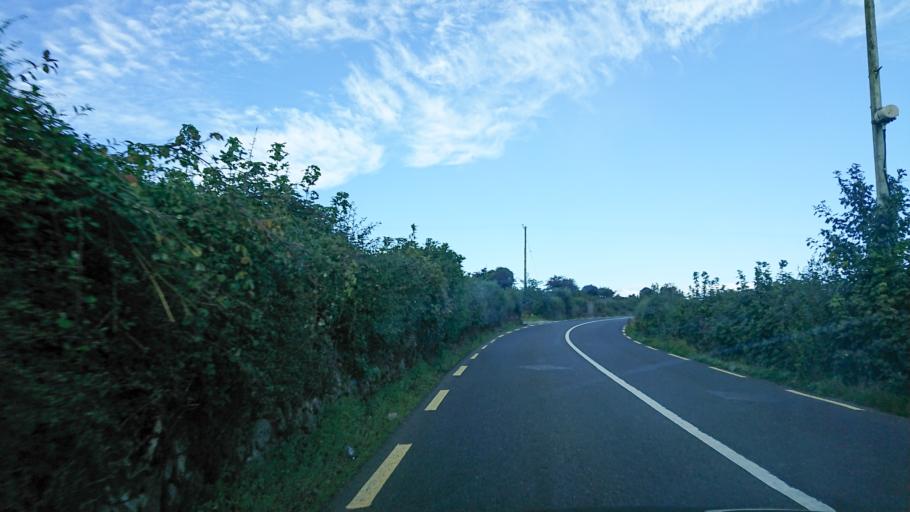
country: IE
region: Munster
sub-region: Waterford
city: Dungarvan
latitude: 52.1348
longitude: -7.6970
